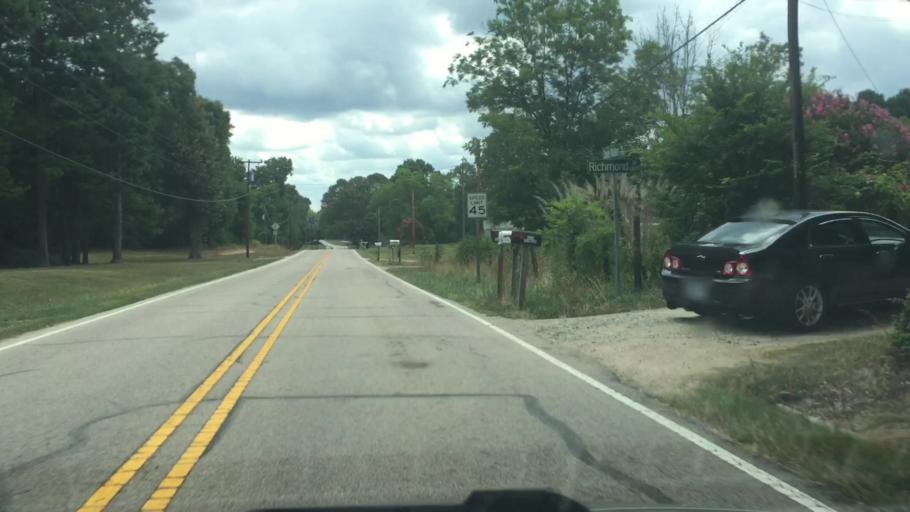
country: US
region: North Carolina
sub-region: Rowan County
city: Enochville
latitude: 35.5054
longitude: -80.6722
